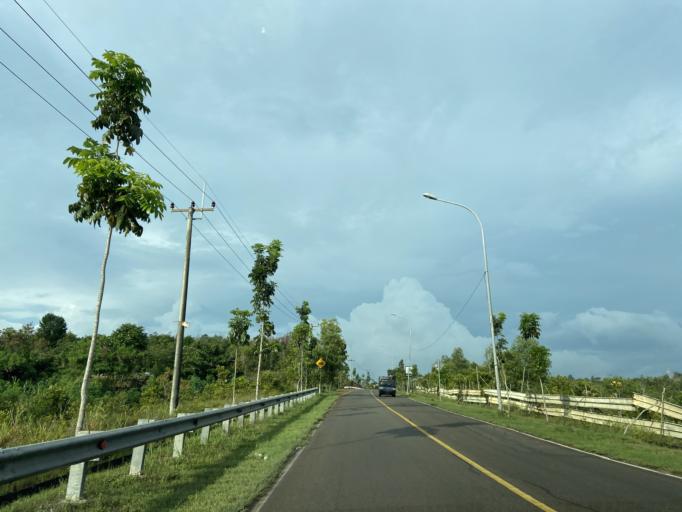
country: ID
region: Riau Islands
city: Tanjungpinang
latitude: 0.9490
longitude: 104.0661
